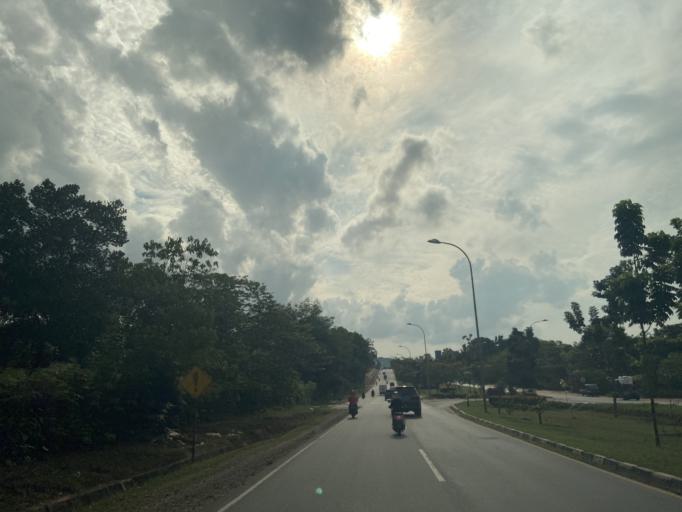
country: SG
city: Singapore
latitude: 1.0991
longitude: 104.0472
